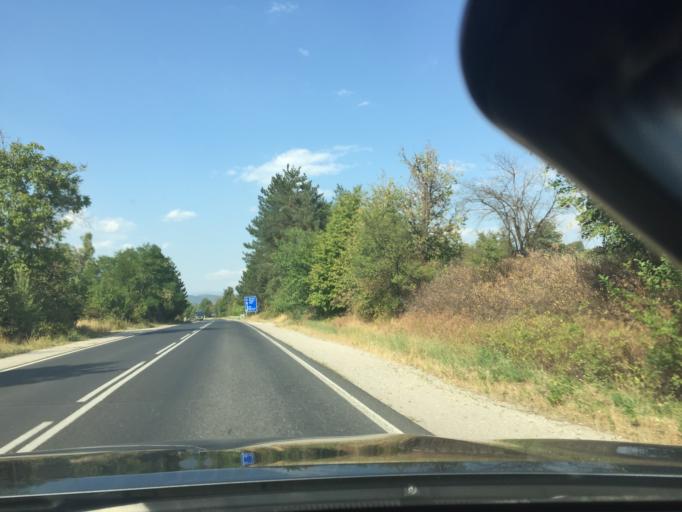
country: BG
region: Kyustendil
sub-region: Obshtina Boboshevo
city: Boboshevo
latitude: 42.2083
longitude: 23.0705
